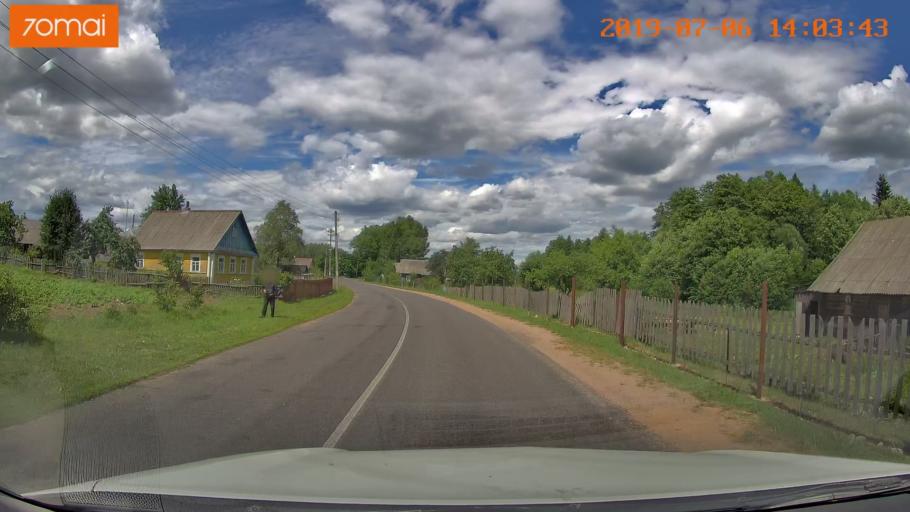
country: BY
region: Minsk
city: Ivyanyets
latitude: 53.8329
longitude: 26.8006
